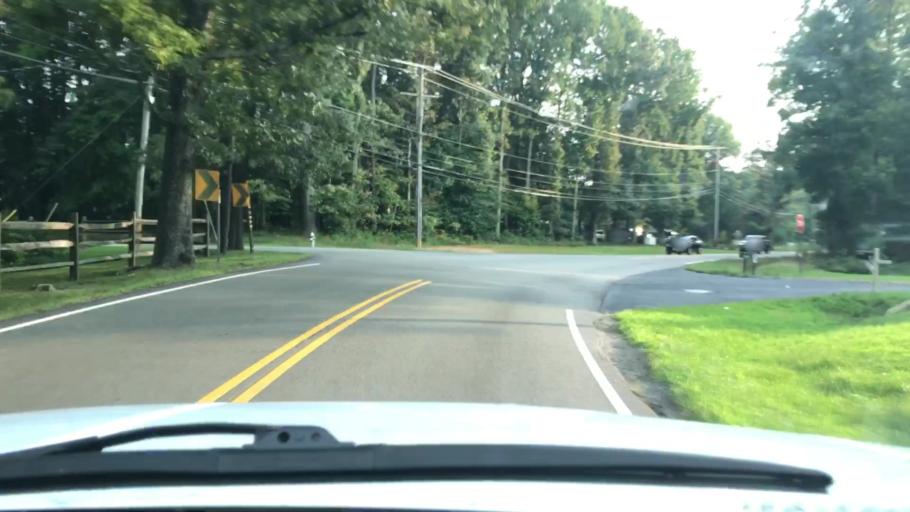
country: US
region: Virginia
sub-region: Chesterfield County
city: Chesterfield
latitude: 37.4347
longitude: -77.5259
